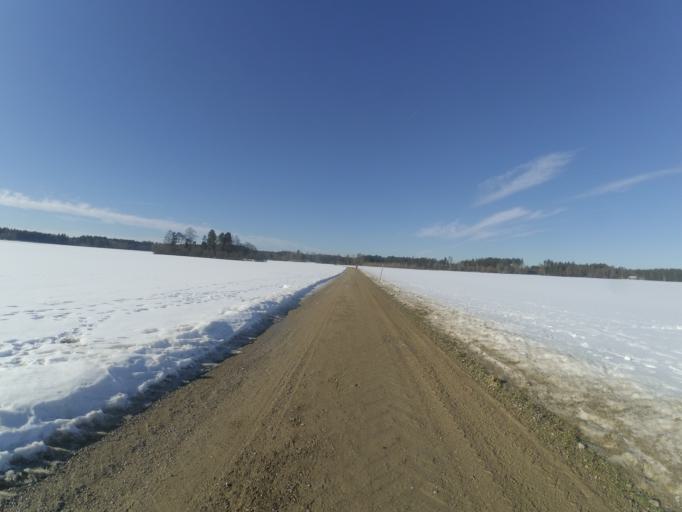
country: DE
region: Bavaria
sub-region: Upper Bavaria
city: Aying
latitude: 47.9777
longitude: 11.7660
